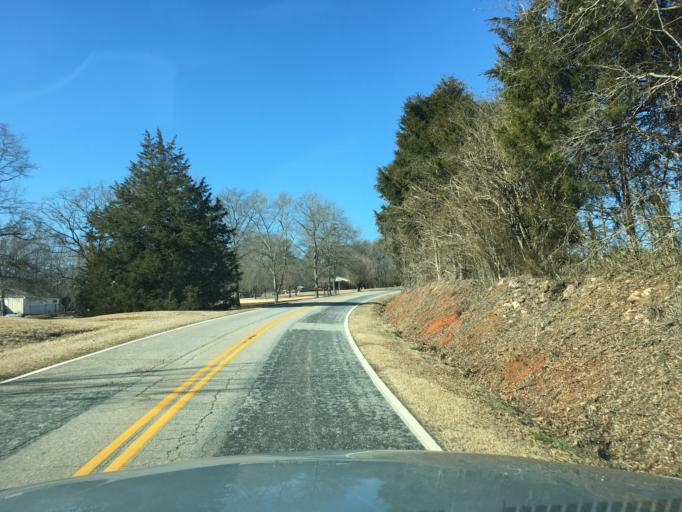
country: US
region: South Carolina
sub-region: Pickens County
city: Pickens
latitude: 34.8584
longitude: -82.7463
